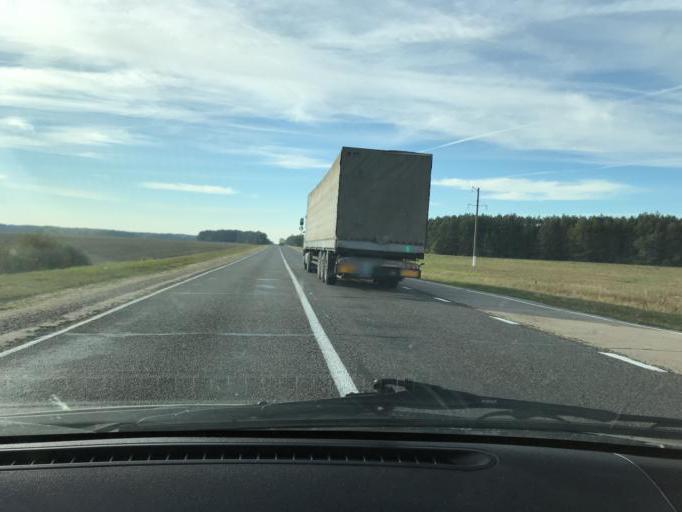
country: BY
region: Brest
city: Lahishyn
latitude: 52.1533
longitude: 25.8158
